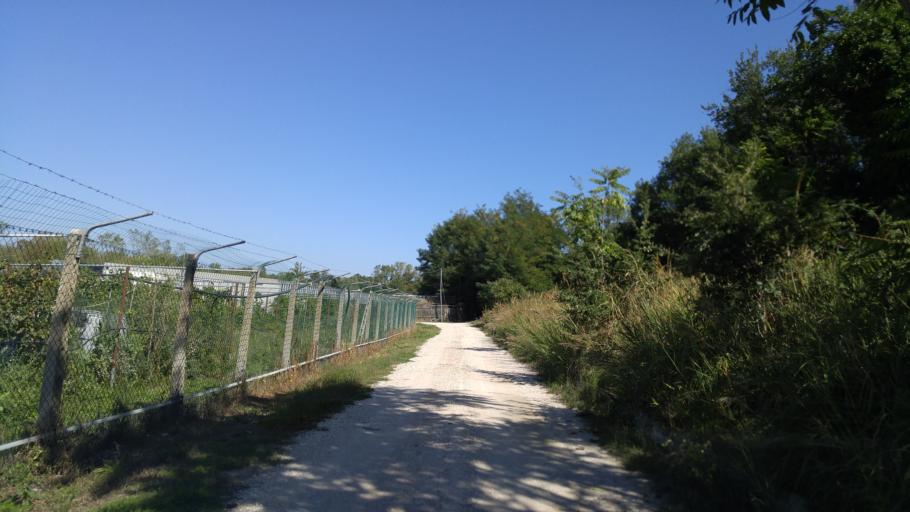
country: IT
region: The Marches
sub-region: Provincia di Pesaro e Urbino
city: Villanova
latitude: 43.7544
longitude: 12.9381
